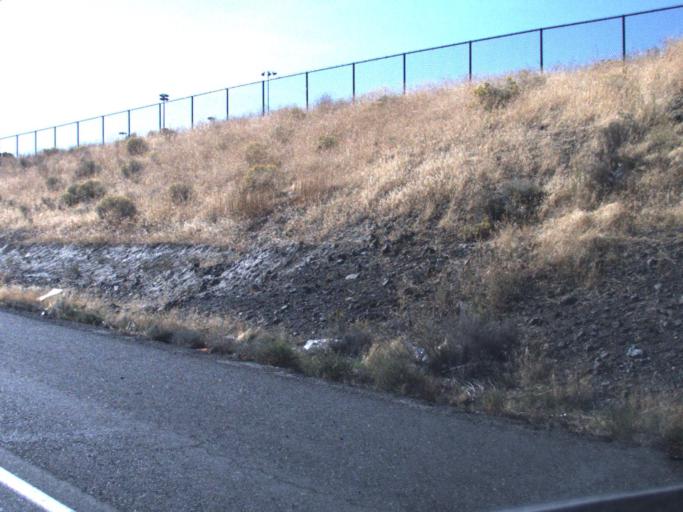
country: US
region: Washington
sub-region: Benton County
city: Kennewick
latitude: 46.1820
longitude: -119.1805
